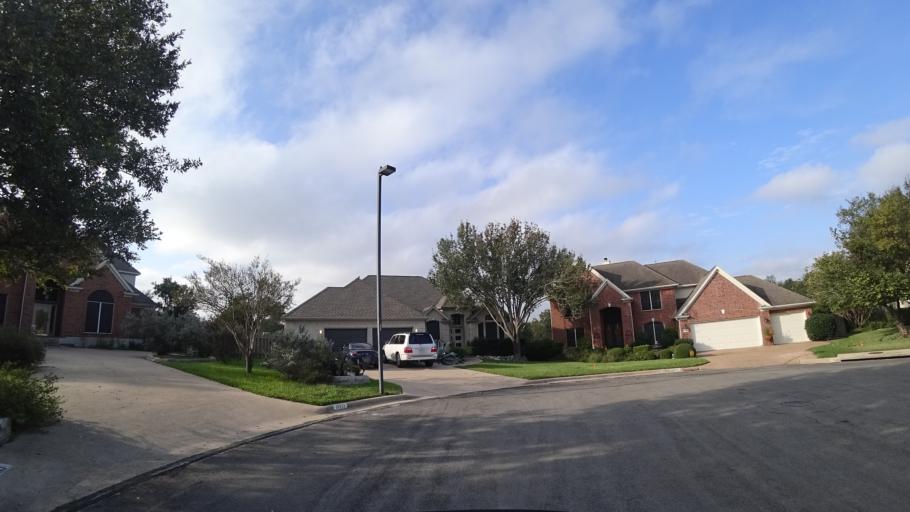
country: US
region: Texas
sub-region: Travis County
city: Shady Hollow
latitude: 30.1923
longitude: -97.8760
